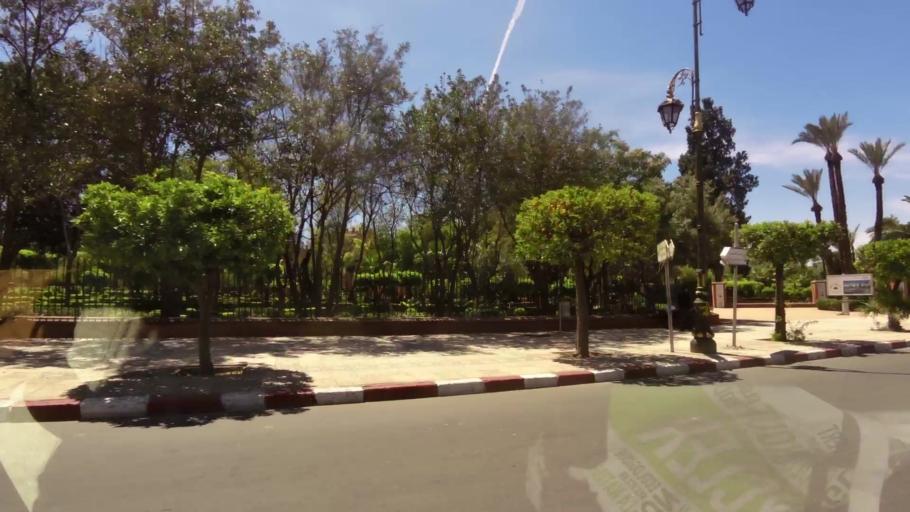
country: MA
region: Marrakech-Tensift-Al Haouz
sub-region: Marrakech
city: Marrakesh
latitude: 31.6271
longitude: -7.9968
